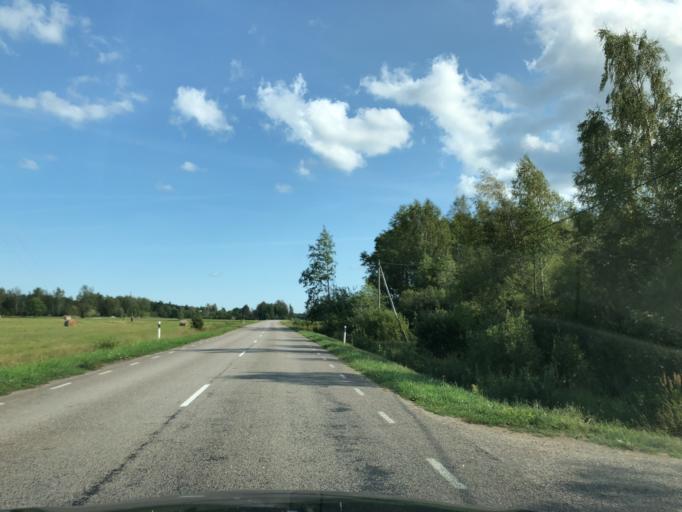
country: EE
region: Hiiumaa
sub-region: Kaerdla linn
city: Kardla
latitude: 58.7178
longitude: 22.5675
